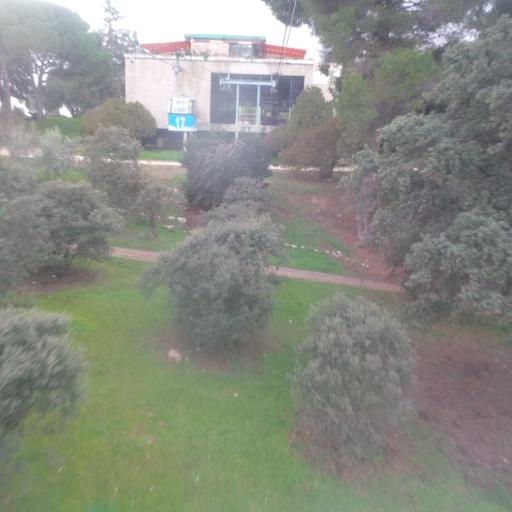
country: ES
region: Madrid
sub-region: Provincia de Madrid
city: Moncloa-Aravaca
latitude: 40.4201
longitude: -3.7479
